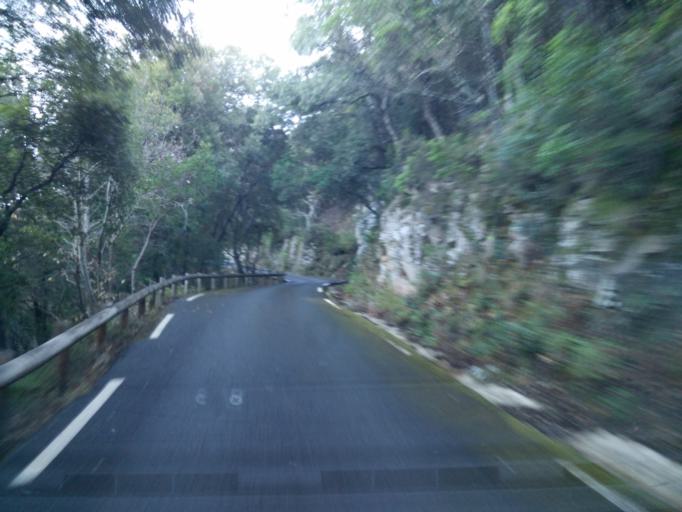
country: FR
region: Provence-Alpes-Cote d'Azur
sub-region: Departement du Var
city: Collobrieres
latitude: 43.2348
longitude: 6.3726
